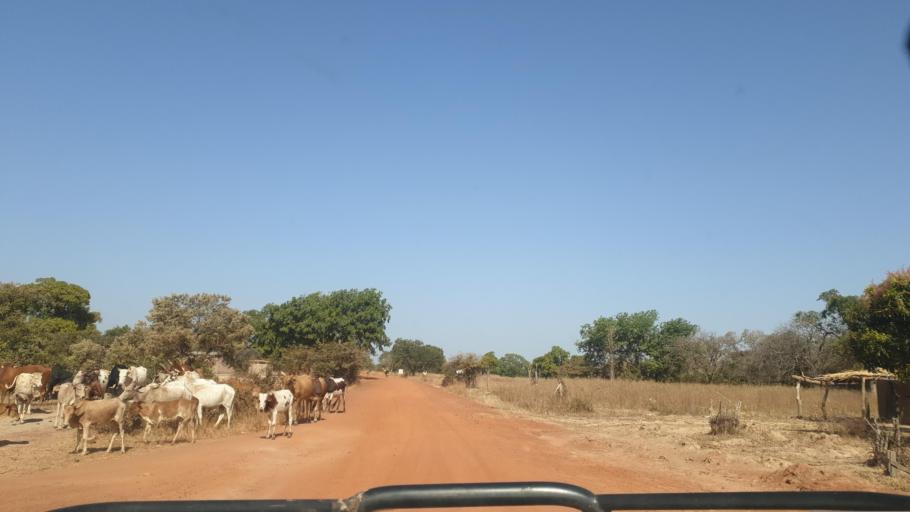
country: ML
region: Sikasso
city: Bougouni
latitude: 11.8150
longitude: -6.9365
